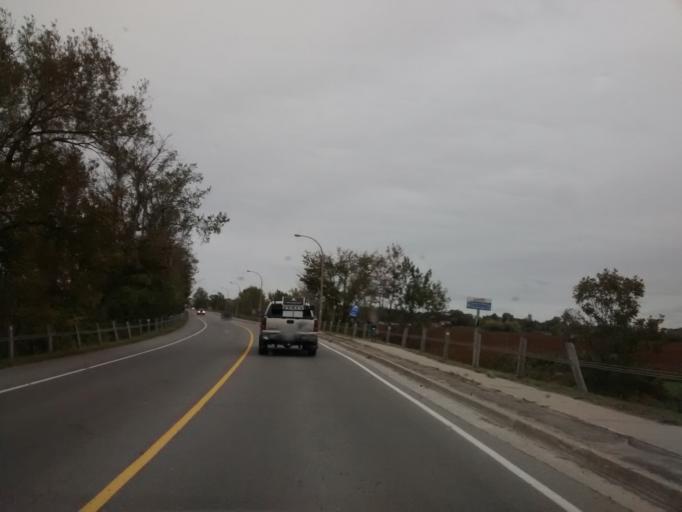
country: CA
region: Ontario
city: Welland
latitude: 42.8956
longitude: -79.6233
